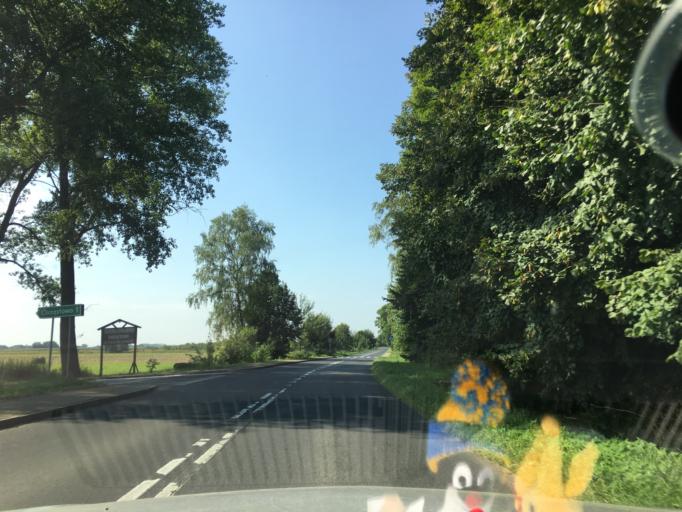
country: PL
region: West Pomeranian Voivodeship
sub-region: Powiat kamienski
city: Kamien Pomorski
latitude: 54.0012
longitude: 14.8352
